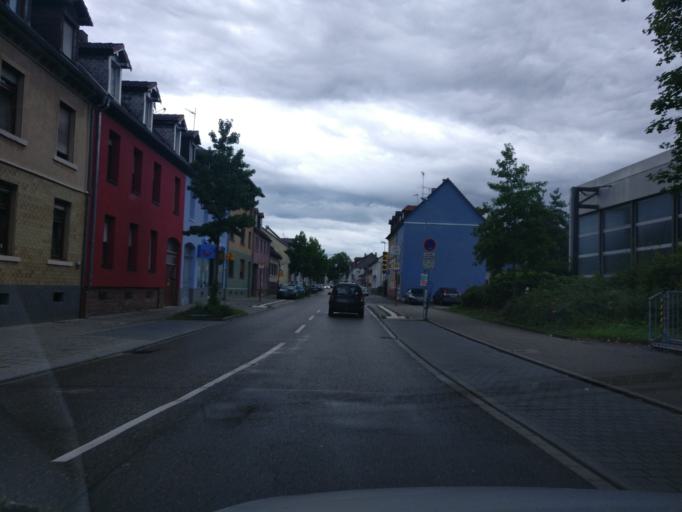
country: DE
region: Baden-Wuerttemberg
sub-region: Karlsruhe Region
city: Weingarten
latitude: 49.0043
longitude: 8.4984
